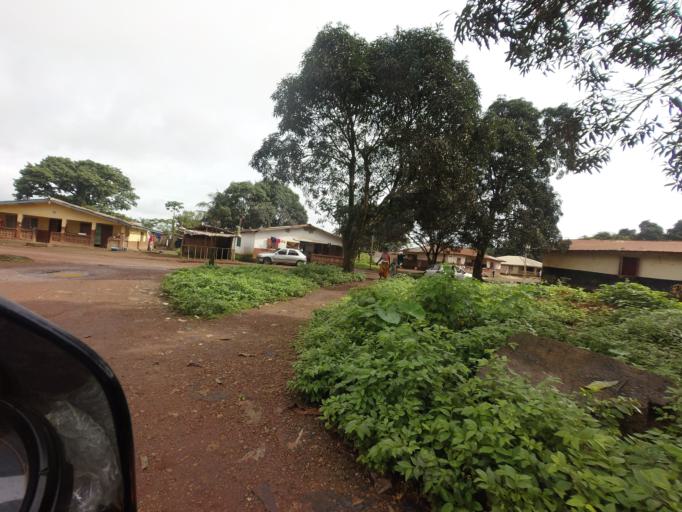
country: SL
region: Northern Province
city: Kambia
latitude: 9.1098
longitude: -12.9284
